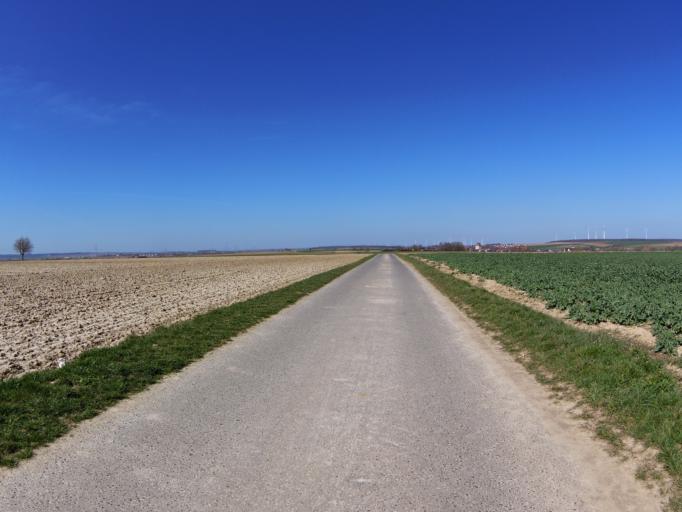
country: DE
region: Bavaria
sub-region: Regierungsbezirk Unterfranken
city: Prosselsheim
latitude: 49.8498
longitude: 10.1233
